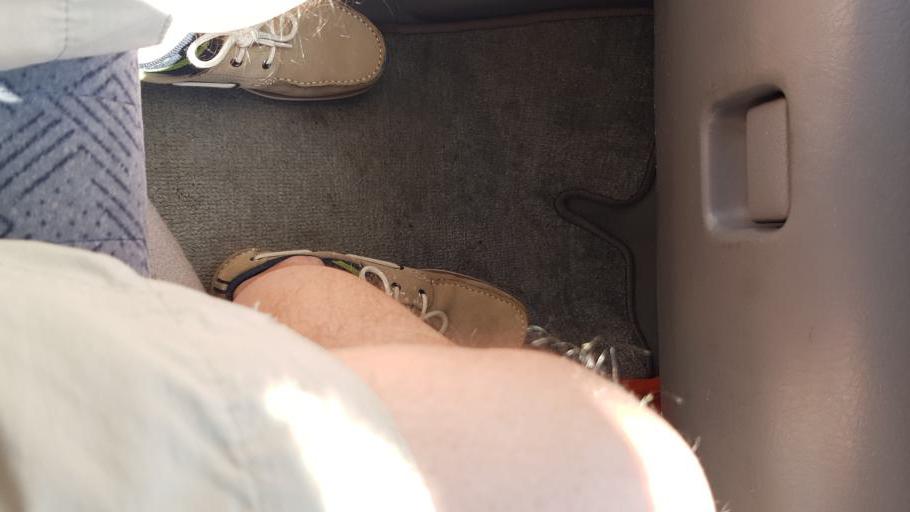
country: GB
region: England
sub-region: Kent
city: Edenbridge
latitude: 51.1869
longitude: 0.1420
